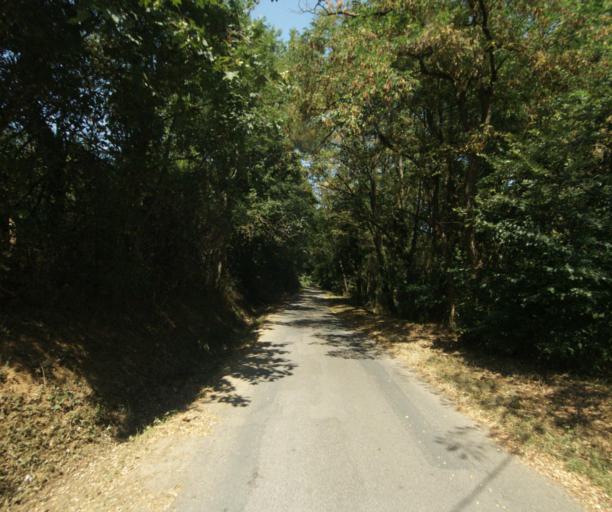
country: FR
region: Rhone-Alpes
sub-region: Departement du Rhone
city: Saint-Pierre-la-Palud
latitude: 45.7988
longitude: 4.6074
